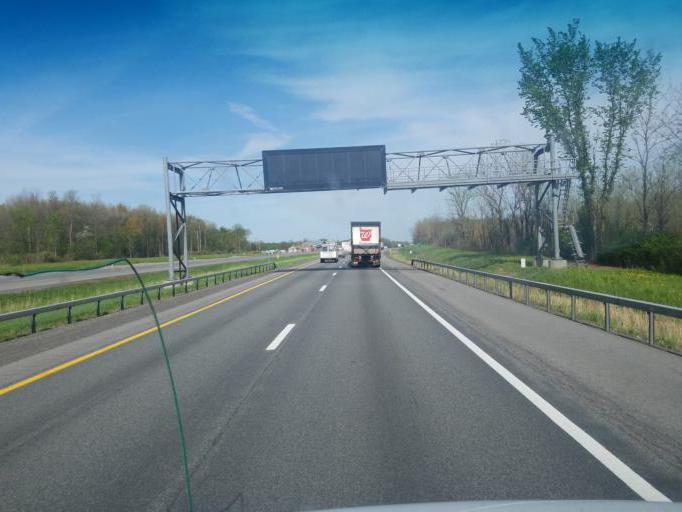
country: US
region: New York
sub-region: Madison County
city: Bolivar
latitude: 43.0956
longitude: -75.8482
